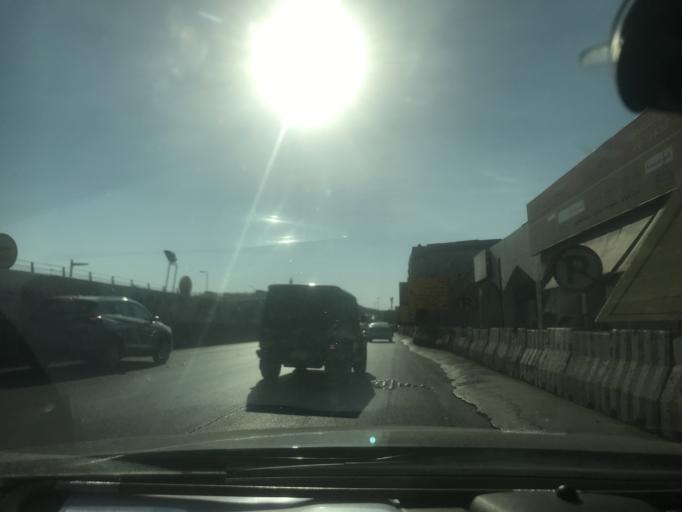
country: SA
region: Ar Riyad
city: Riyadh
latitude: 24.6243
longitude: 46.7079
